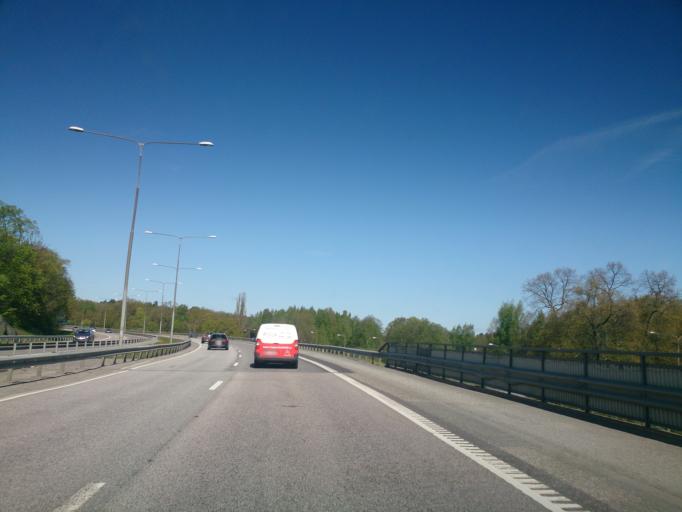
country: SE
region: Stockholm
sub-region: Nacka Kommun
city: Alta
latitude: 59.2416
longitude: 18.1193
